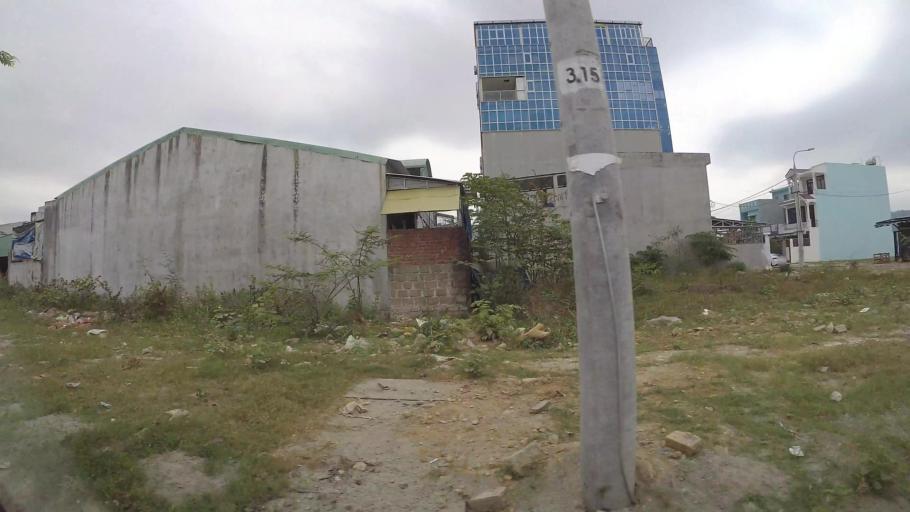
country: VN
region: Da Nang
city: Lien Chieu
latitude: 16.0486
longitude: 108.1669
